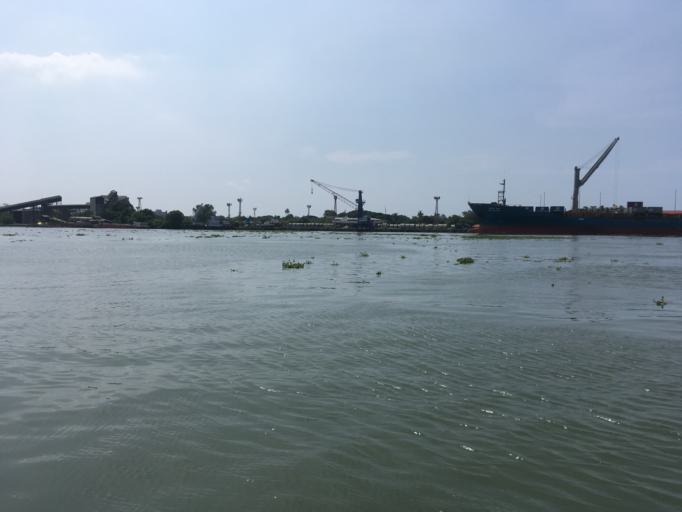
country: IN
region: Kerala
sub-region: Ernakulam
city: Cochin
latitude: 9.9699
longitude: 76.2710
